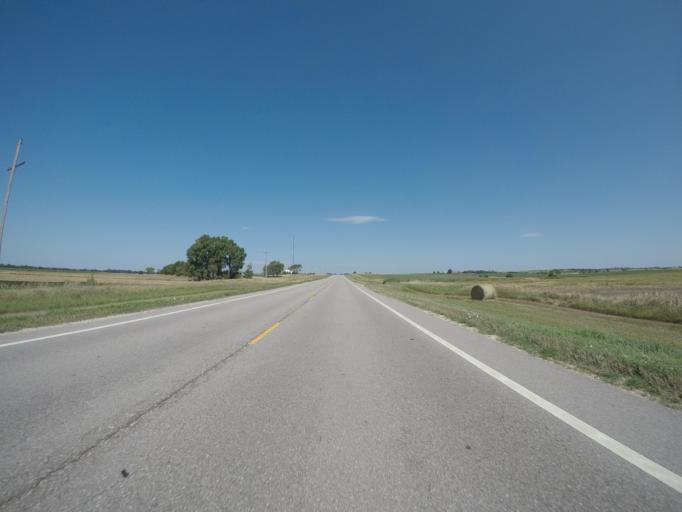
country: US
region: Kansas
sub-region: Cloud County
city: Concordia
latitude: 39.3716
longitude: -97.8417
